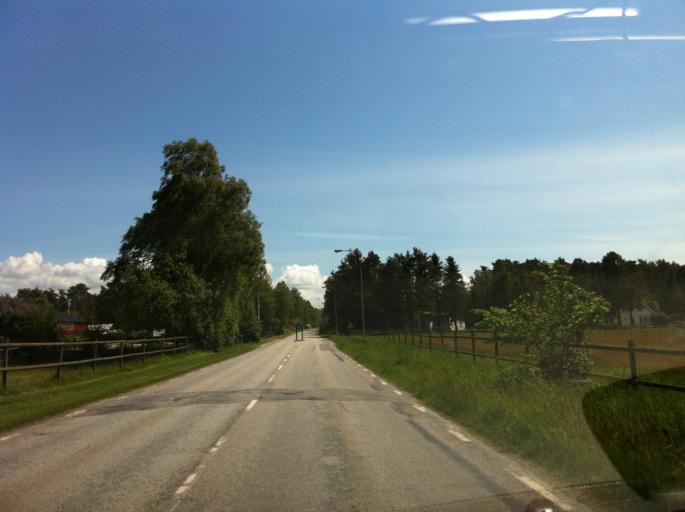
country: SE
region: Skane
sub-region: Kavlinge Kommun
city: Hofterup
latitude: 55.8044
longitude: 12.9842
